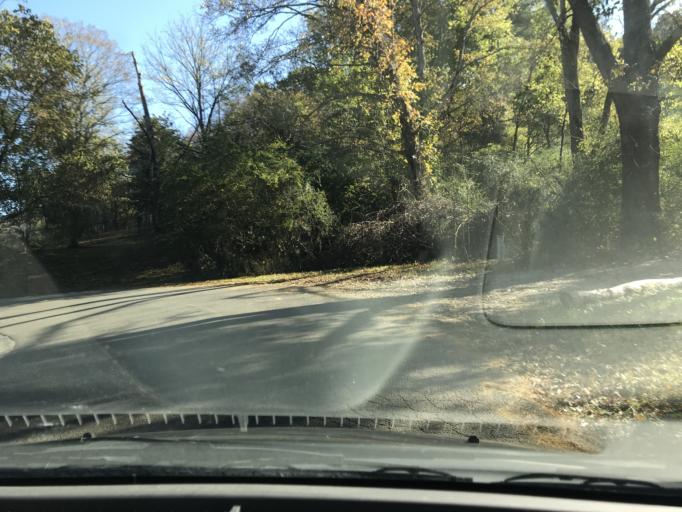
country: US
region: Georgia
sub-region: Dade County
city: Trenton
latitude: 34.8948
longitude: -85.4638
